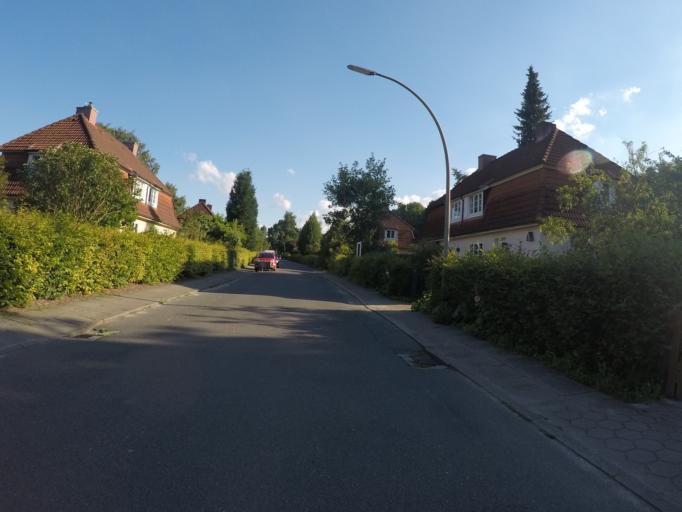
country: DE
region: Hamburg
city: Langenhorn
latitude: 53.6594
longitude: 10.0178
